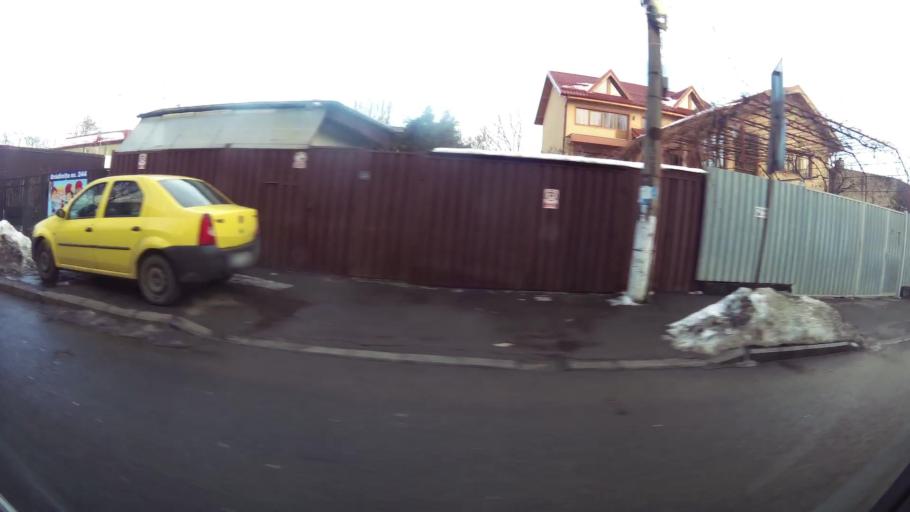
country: RO
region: Bucuresti
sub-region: Municipiul Bucuresti
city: Bucuresti
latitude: 44.3947
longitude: 26.0700
